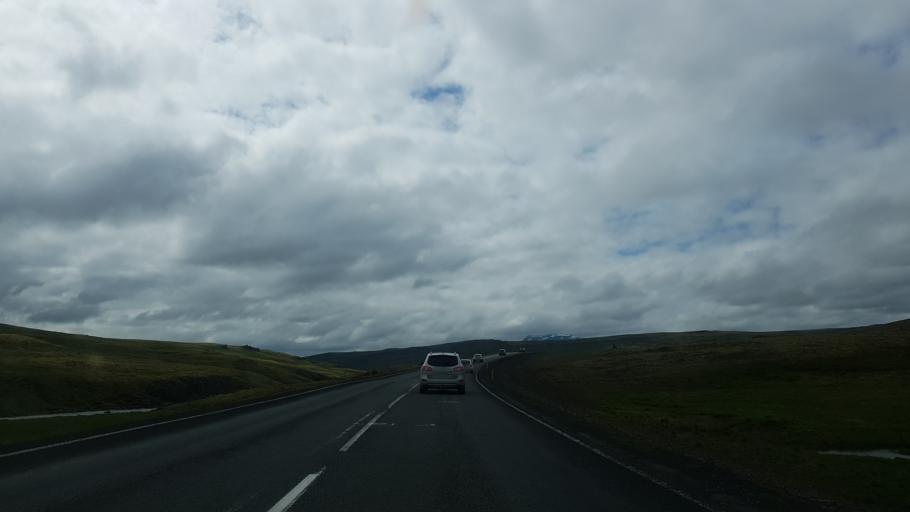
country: IS
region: West
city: Borgarnes
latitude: 64.9113
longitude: -21.1493
